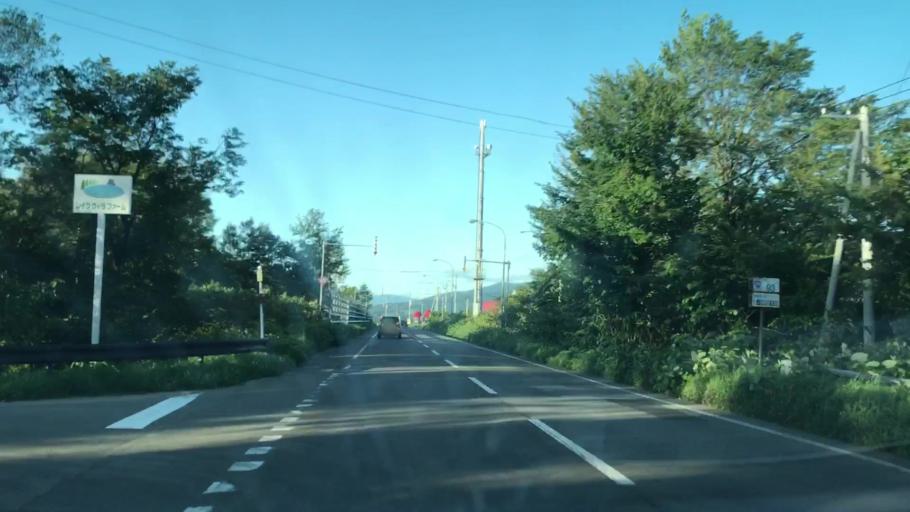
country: JP
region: Hokkaido
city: Date
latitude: 42.6243
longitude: 140.7969
